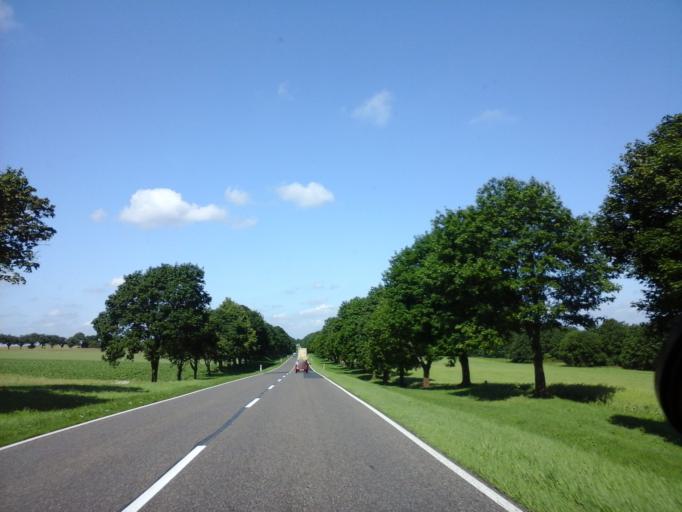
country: PL
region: West Pomeranian Voivodeship
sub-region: Powiat stargardzki
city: Suchan
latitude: 53.2744
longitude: 15.4044
